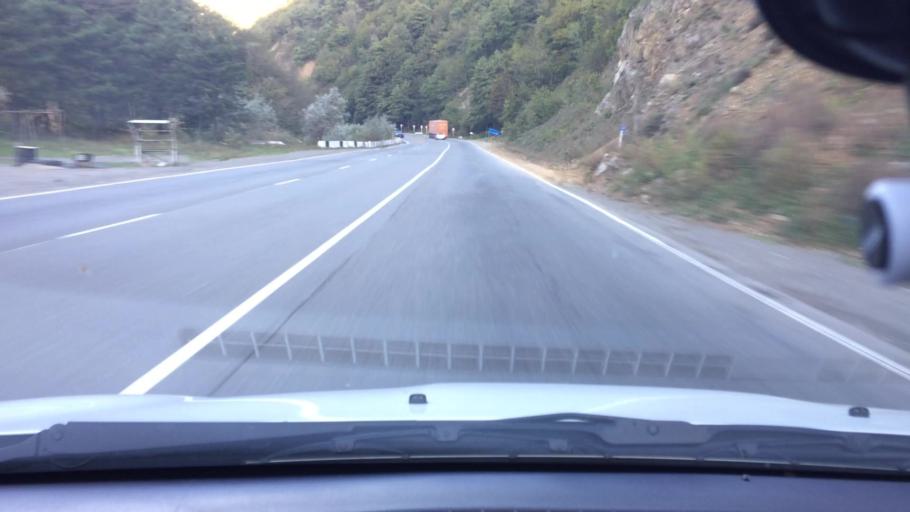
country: GE
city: Surami
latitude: 42.0926
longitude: 43.4617
